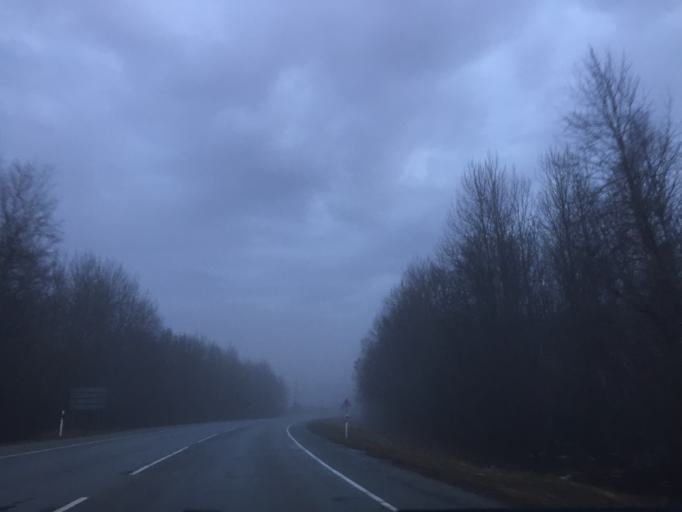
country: EE
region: Laeaene
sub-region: Lihula vald
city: Lihula
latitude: 58.6827
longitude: 23.8119
